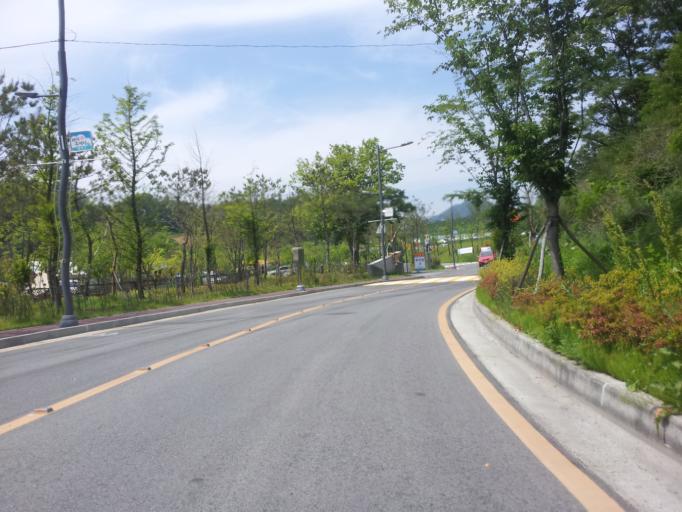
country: KR
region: Daejeon
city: Sintansin
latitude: 36.4559
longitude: 127.4754
